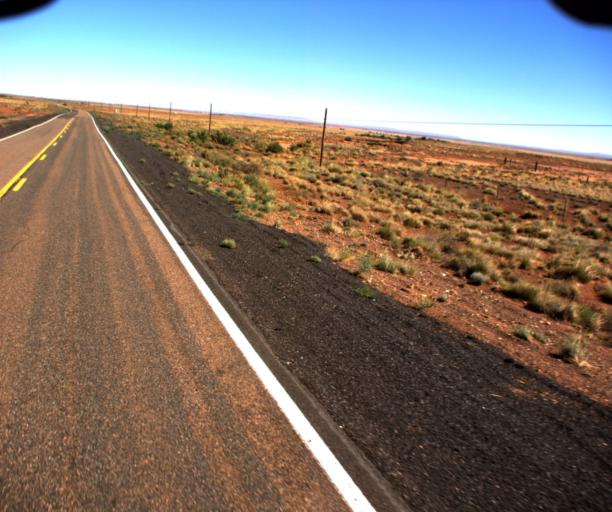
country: US
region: Arizona
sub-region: Coconino County
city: LeChee
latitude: 35.1407
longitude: -110.8912
